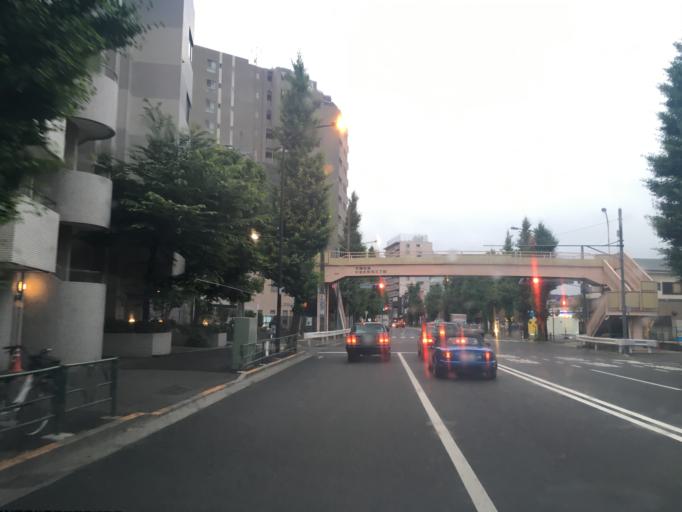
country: JP
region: Tokyo
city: Tokyo
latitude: 35.7025
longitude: 139.6287
